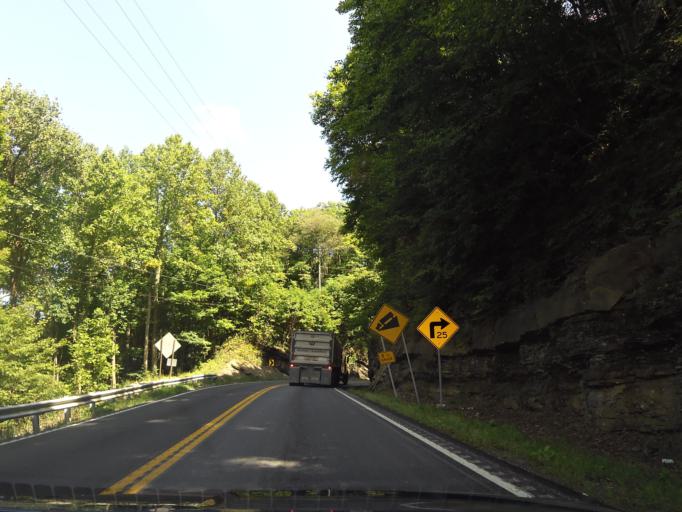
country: US
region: Kentucky
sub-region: Harlan County
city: Harlan
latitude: 36.8991
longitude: -83.3110
